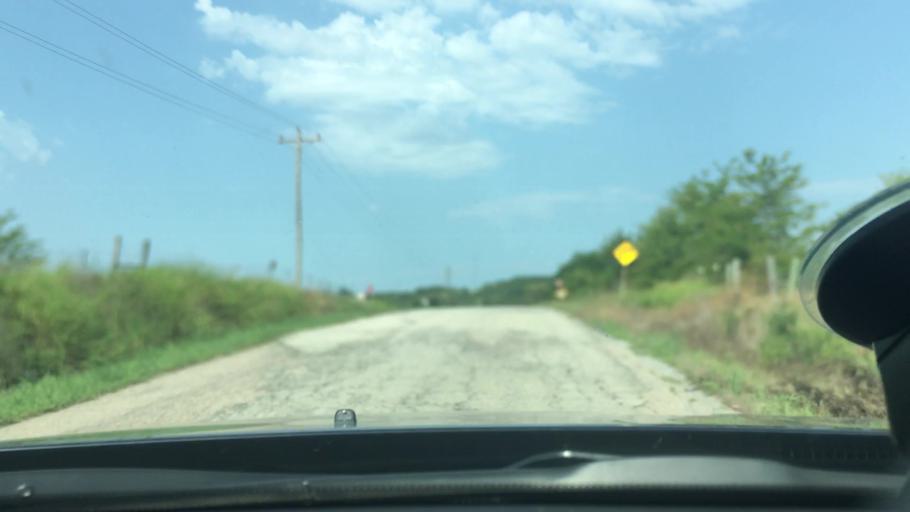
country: US
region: Oklahoma
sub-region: Atoka County
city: Atoka
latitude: 34.4616
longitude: -96.0389
